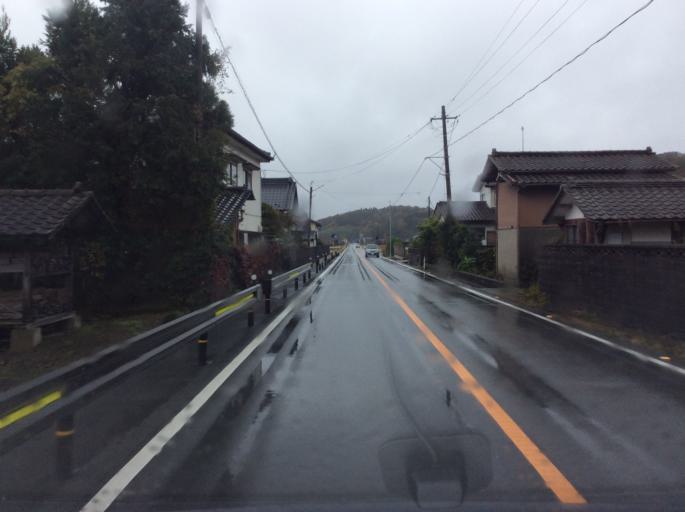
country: JP
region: Fukushima
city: Iwaki
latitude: 37.1054
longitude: 140.9535
